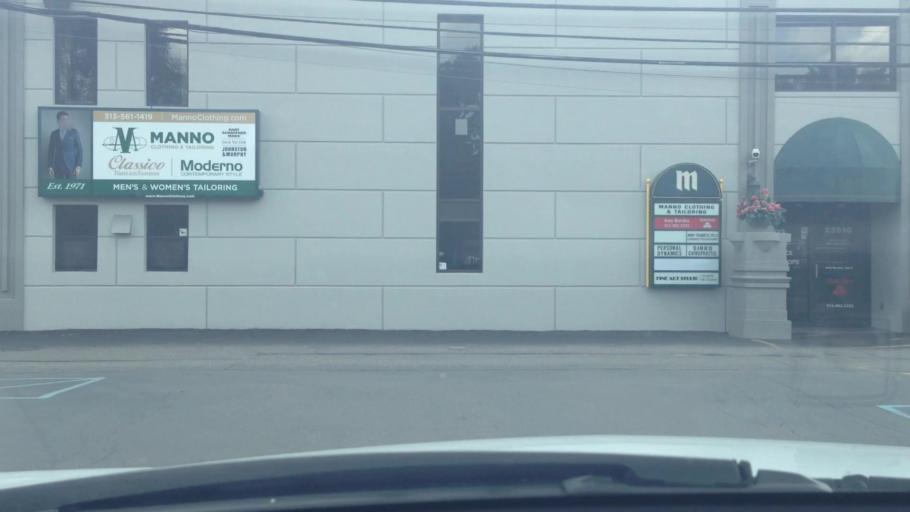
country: US
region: Michigan
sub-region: Wayne County
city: Dearborn Heights
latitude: 42.3011
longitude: -83.2691
